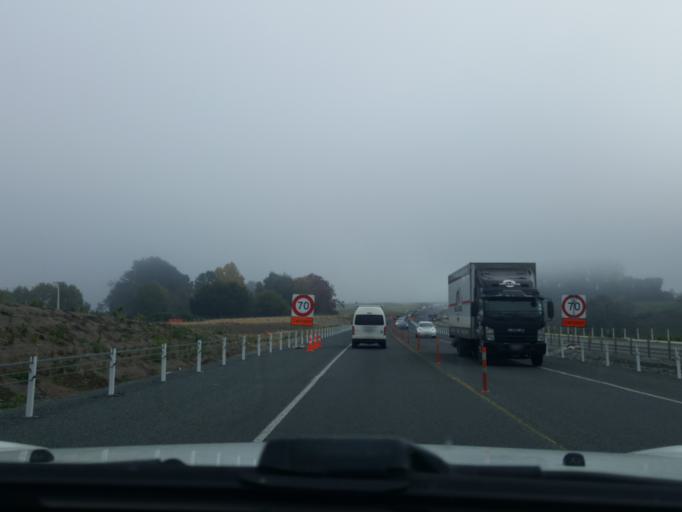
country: NZ
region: Waikato
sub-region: Waikato District
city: Te Kauwhata
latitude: -37.3985
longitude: 175.1146
